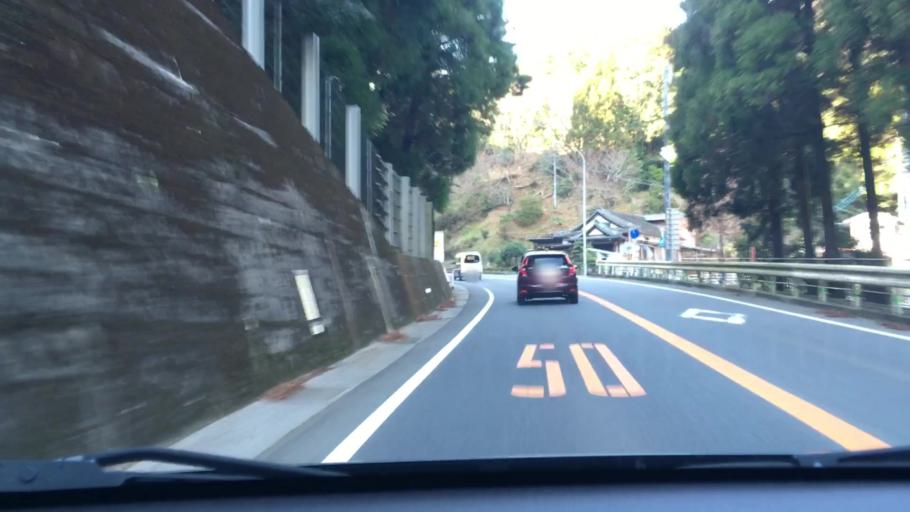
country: JP
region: Oita
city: Tsukumiura
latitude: 32.9998
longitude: 131.8135
